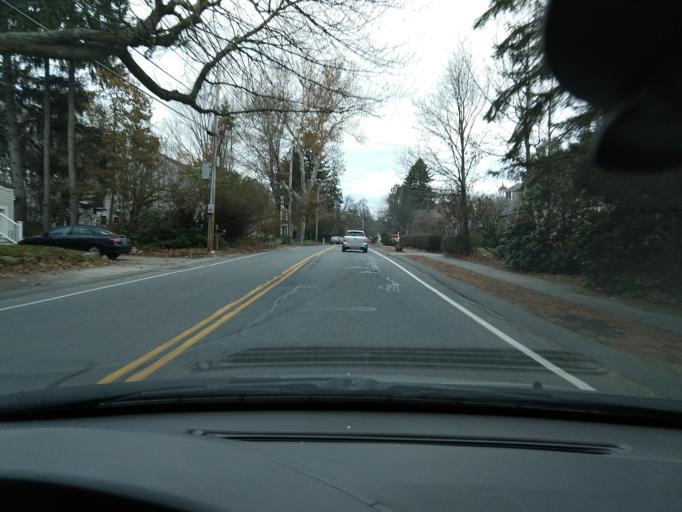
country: US
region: Massachusetts
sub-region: Middlesex County
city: Westford
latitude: 42.5791
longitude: -71.4372
